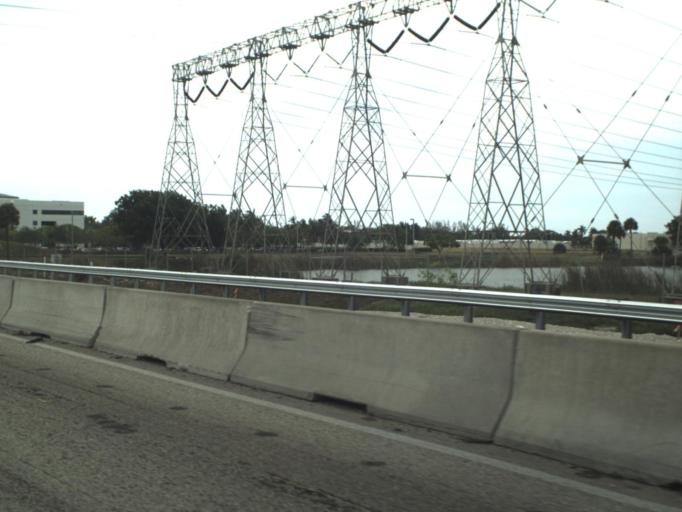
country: US
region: Florida
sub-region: Broward County
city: Dania Beach
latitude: 26.0554
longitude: -80.1621
